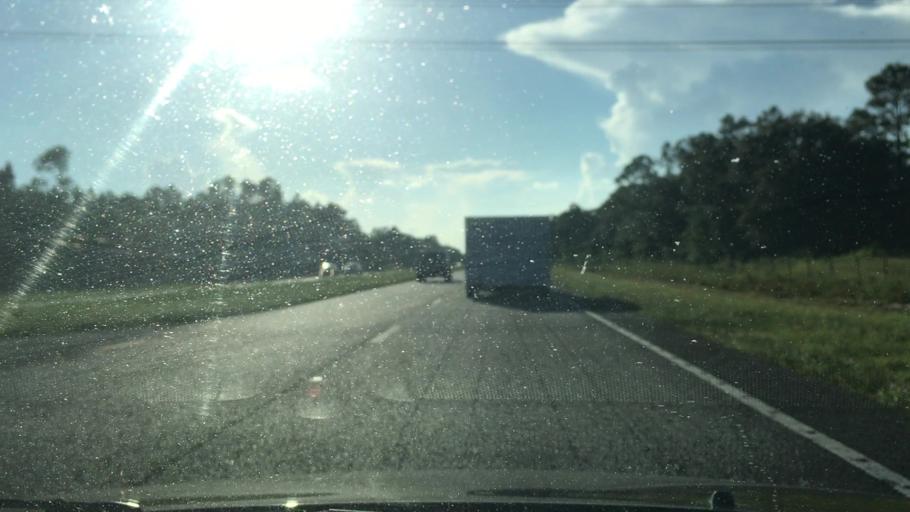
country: US
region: Florida
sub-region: Orange County
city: Christmas
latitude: 28.5364
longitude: -81.0571
